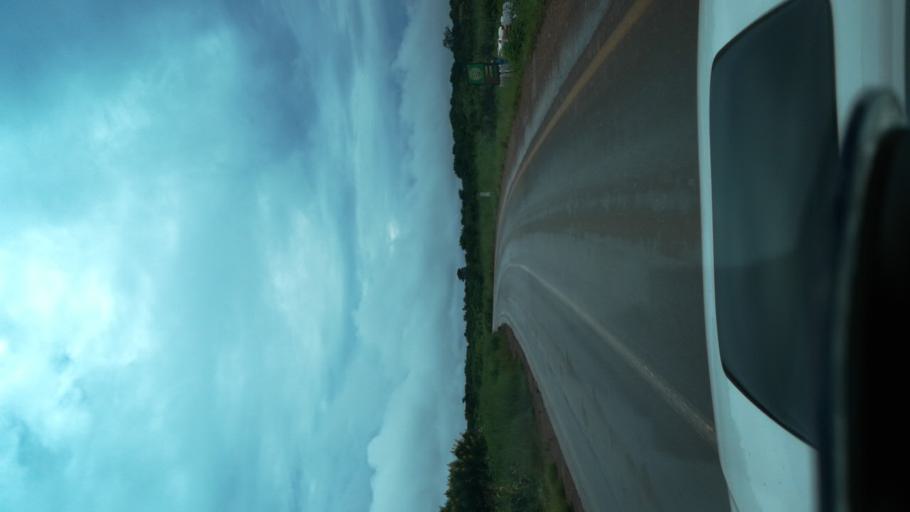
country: CD
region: Katanga
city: Lubumbashi
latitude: -11.5415
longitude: 27.6104
